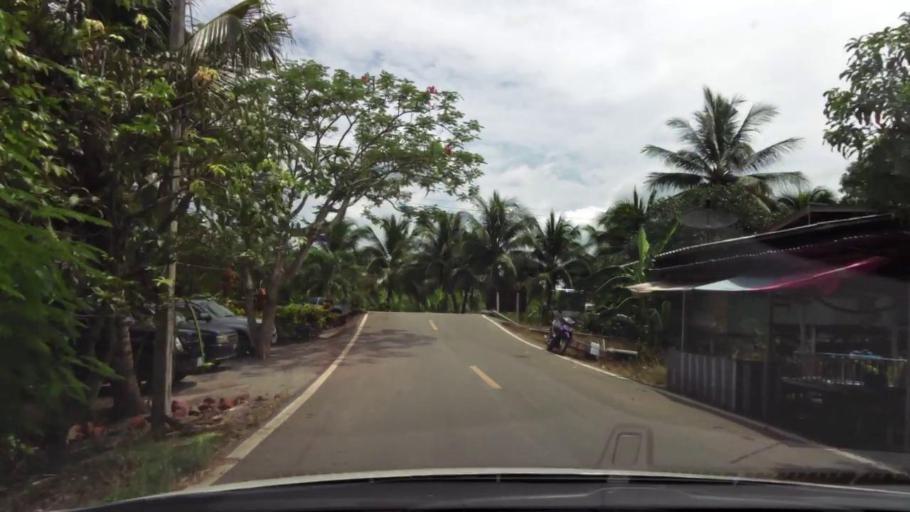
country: TH
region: Ratchaburi
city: Damnoen Saduak
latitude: 13.5206
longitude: 100.0131
